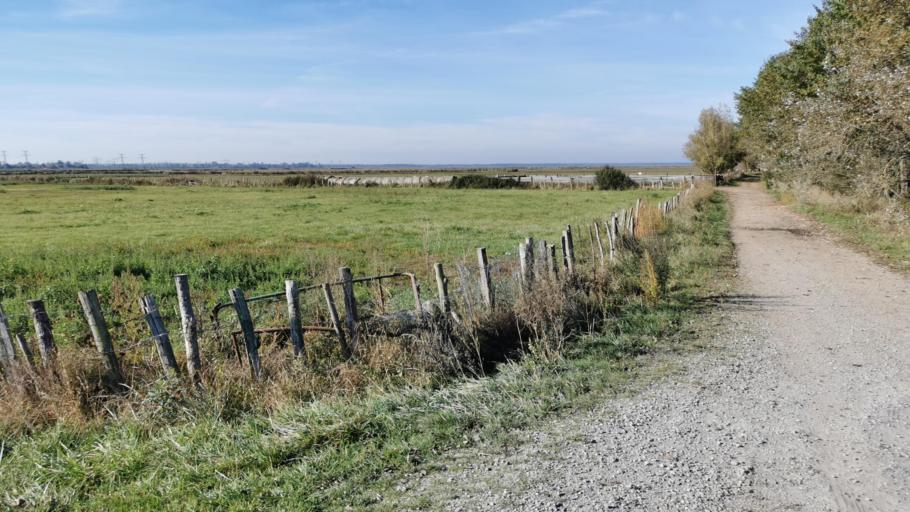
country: FR
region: Pays de la Loire
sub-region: Departement de la Loire-Atlantique
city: Saint-Malo-de-Guersac
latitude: 47.3407
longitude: -2.1906
